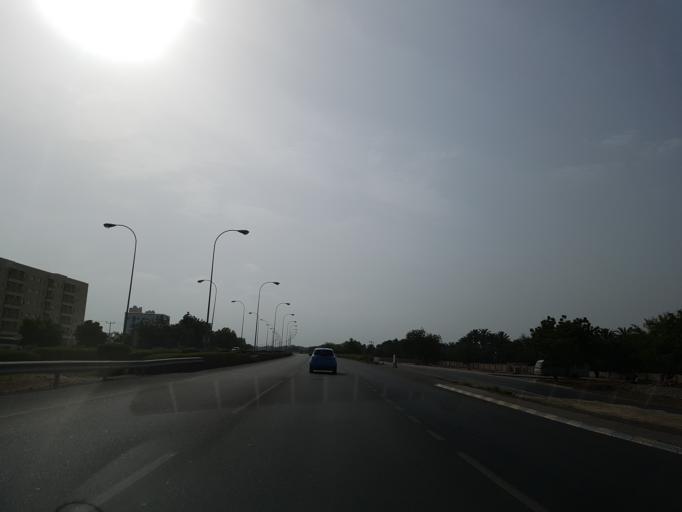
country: OM
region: Al Batinah
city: Al Sohar
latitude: 24.3988
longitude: 56.6671
